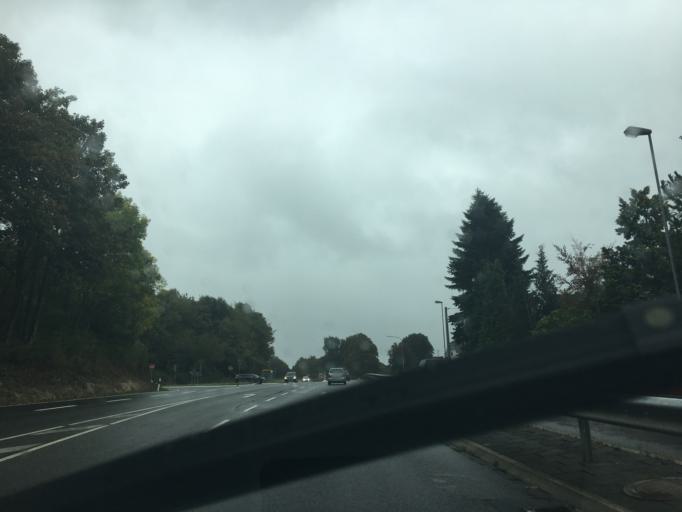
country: DE
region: Rheinland-Pfalz
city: Montabaur
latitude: 50.4367
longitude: 7.8386
